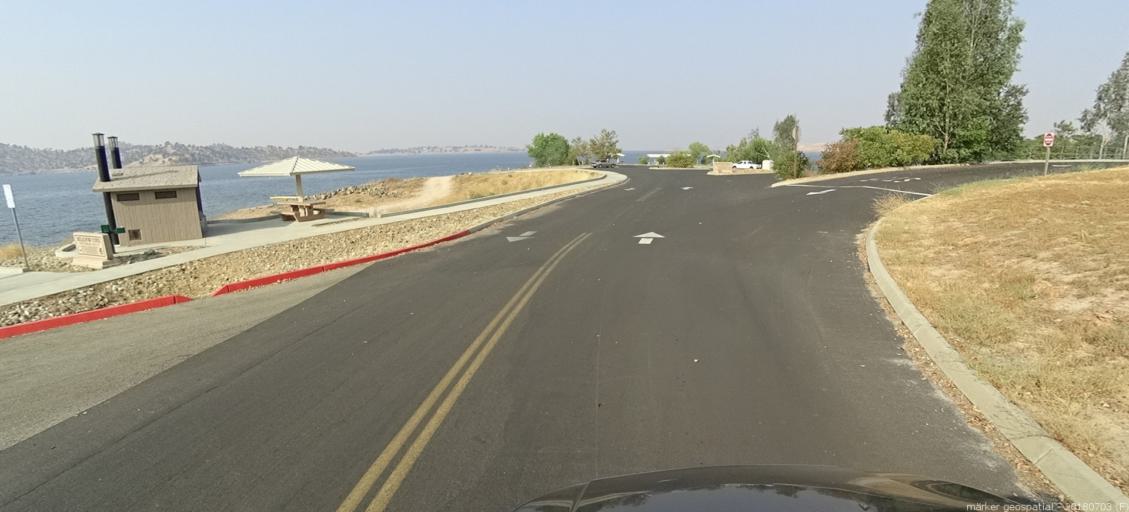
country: US
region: California
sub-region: Fresno County
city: Auberry
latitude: 37.0182
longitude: -119.6677
